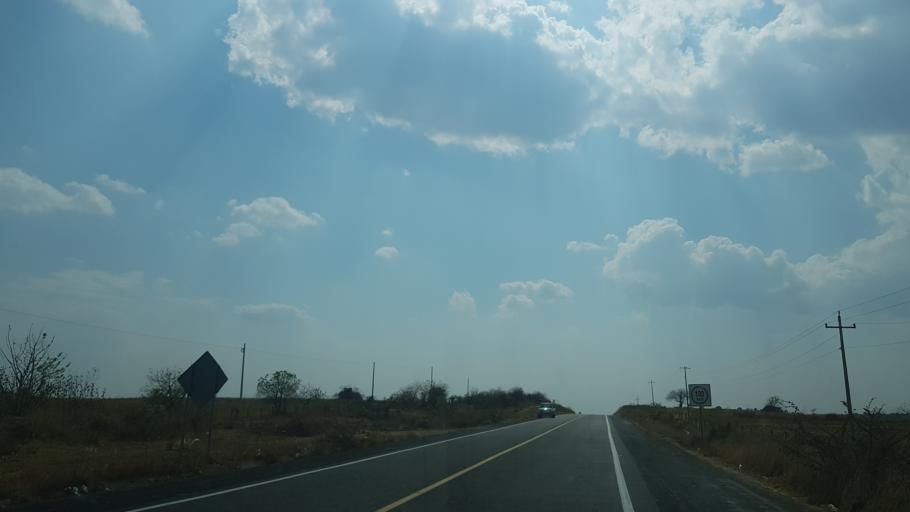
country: MX
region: Puebla
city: San Juan Amecac
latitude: 18.8171
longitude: -98.6545
